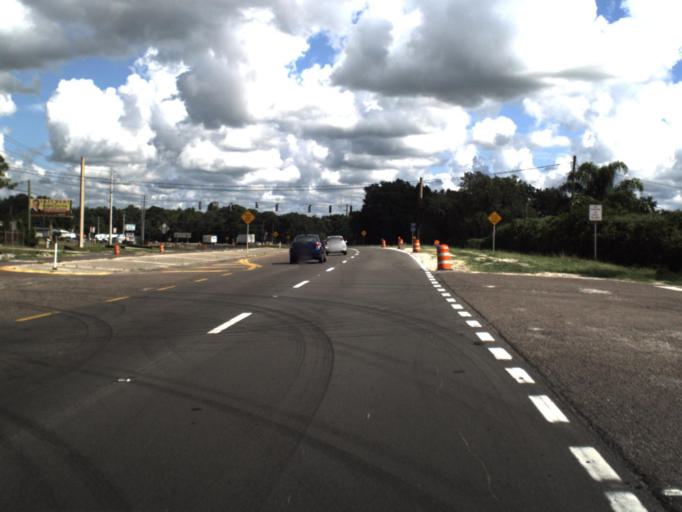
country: US
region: Florida
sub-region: Polk County
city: Gibsonia
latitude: 28.1610
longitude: -81.9736
